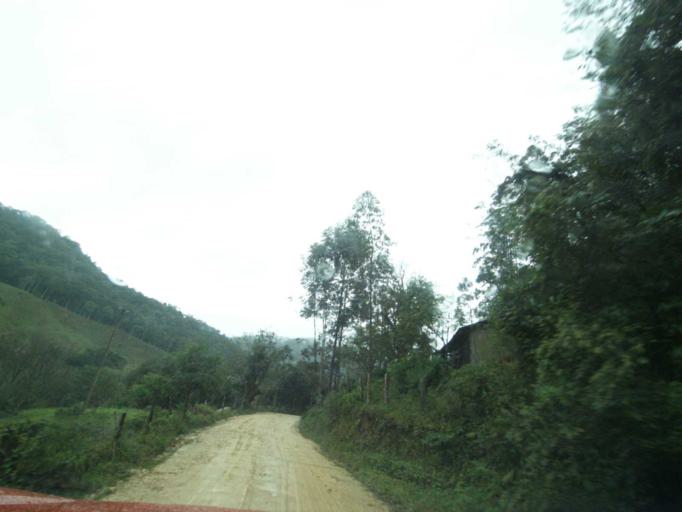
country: BR
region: Santa Catarina
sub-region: Anitapolis
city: Anitapolis
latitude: -27.9156
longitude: -49.1918
